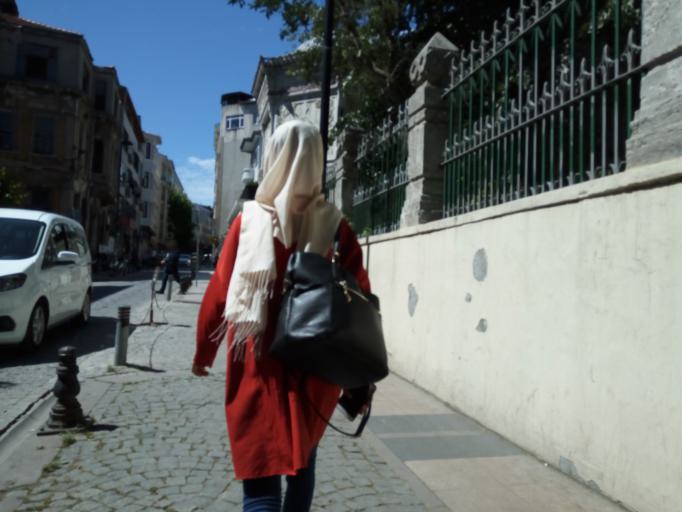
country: TR
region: Istanbul
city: Eminoenue
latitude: 41.0064
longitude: 28.9729
